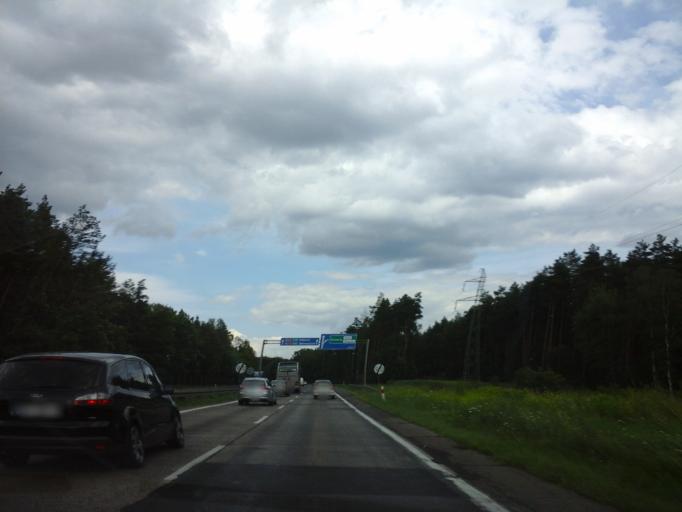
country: PL
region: West Pomeranian Voivodeship
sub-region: Powiat gryfinski
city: Stare Czarnowo
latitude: 53.3795
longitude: 14.7083
